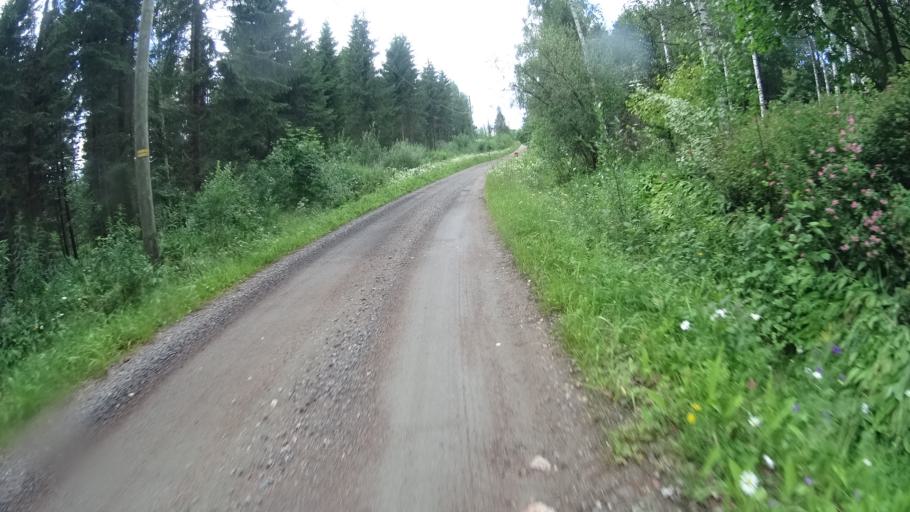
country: FI
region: Uusimaa
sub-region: Helsinki
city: Karkkila
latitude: 60.6062
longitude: 24.1903
